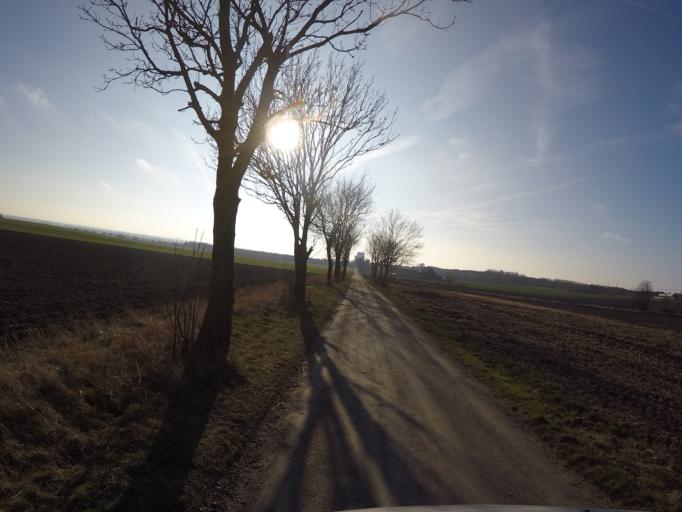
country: SE
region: Skane
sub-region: Lunds Kommun
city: Lund
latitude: 55.6955
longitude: 13.2603
